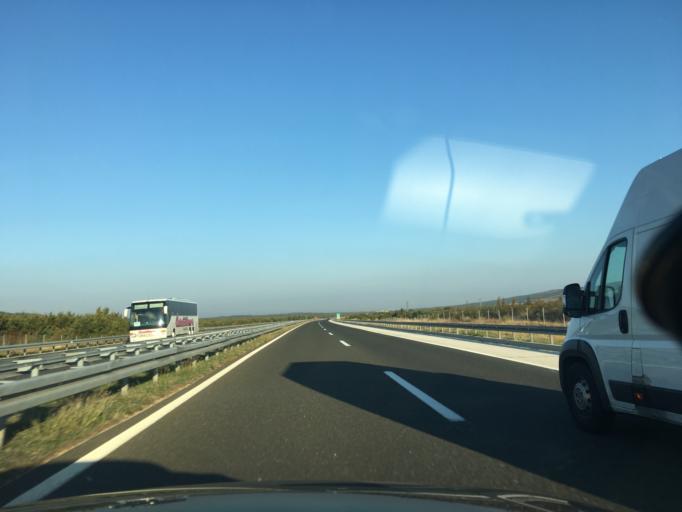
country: HR
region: Sibensko-Kniniska
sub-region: Grad Sibenik
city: Pirovac
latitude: 43.9277
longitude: 15.7216
